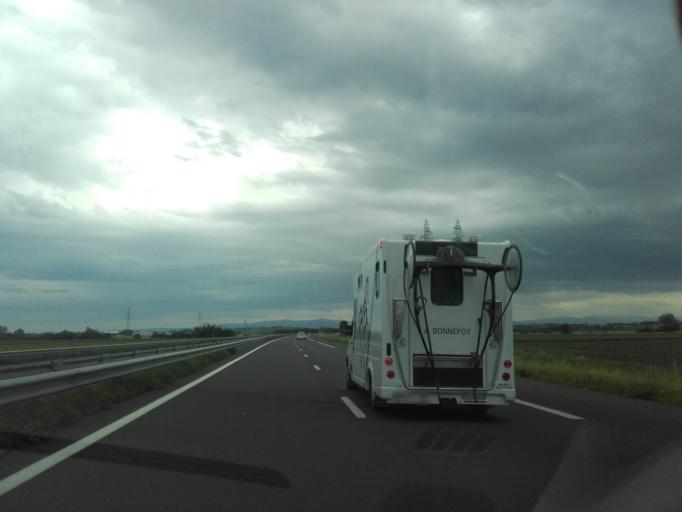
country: FR
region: Auvergne
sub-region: Departement du Puy-de-Dome
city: Malintrat
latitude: 45.8244
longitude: 3.1991
